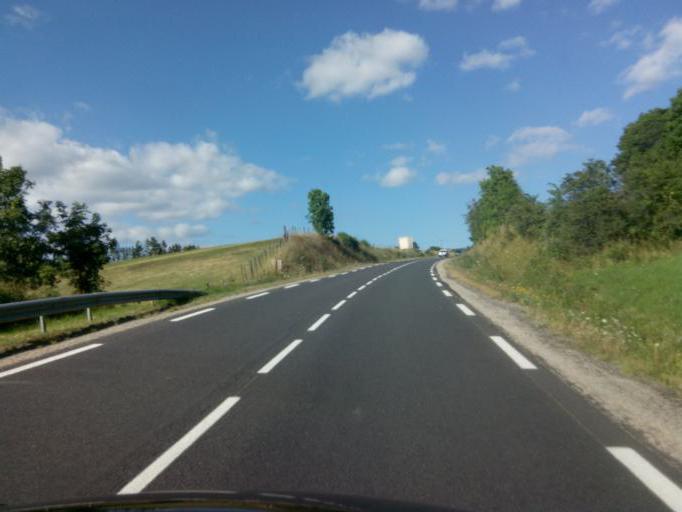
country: FR
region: Auvergne
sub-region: Departement de la Haute-Loire
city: Saint-Paulien
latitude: 45.1578
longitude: 3.8260
